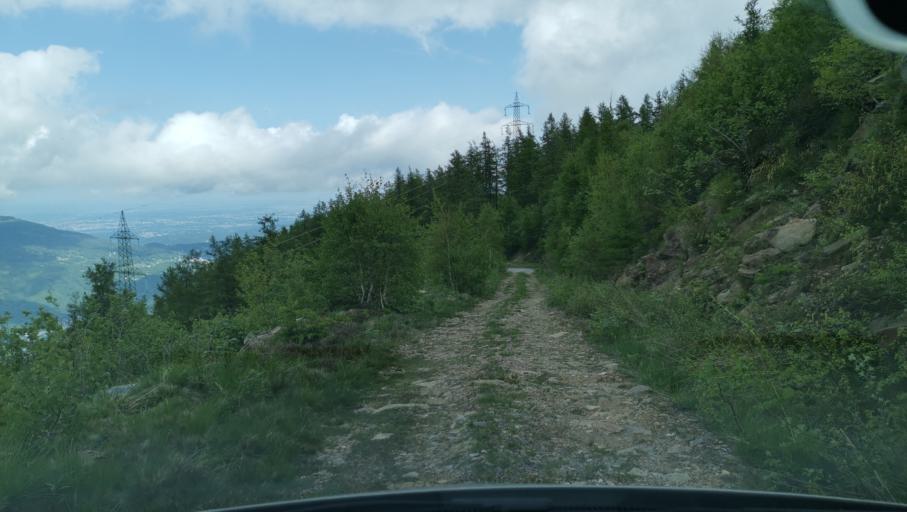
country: IT
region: Piedmont
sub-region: Provincia di Torino
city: Tavagnasco
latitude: 45.5329
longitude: 7.7935
